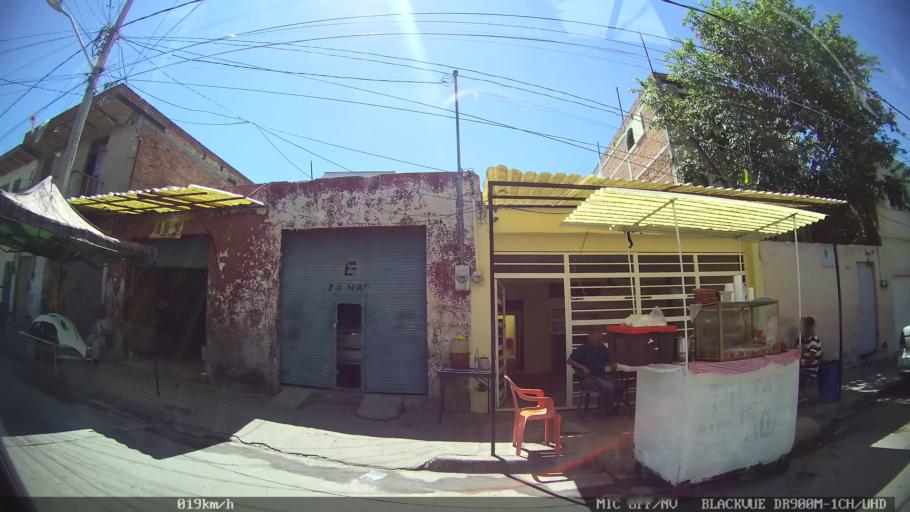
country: MX
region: Jalisco
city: Tlaquepaque
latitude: 20.6890
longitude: -103.2913
